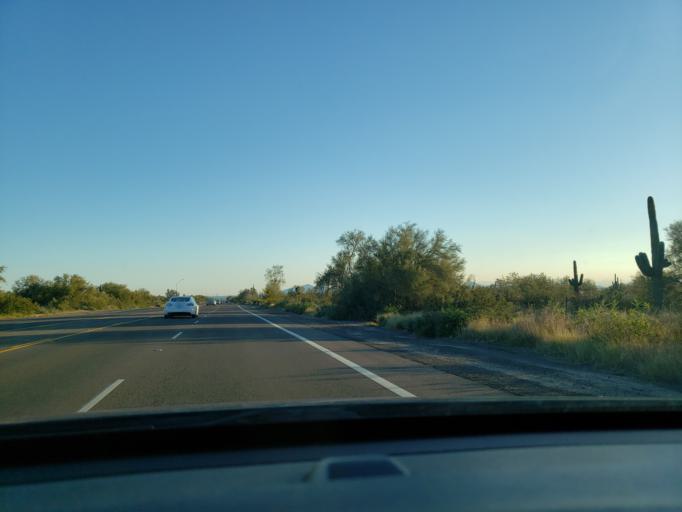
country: US
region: Arizona
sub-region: Maricopa County
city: Carefree
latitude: 33.7120
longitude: -111.9254
